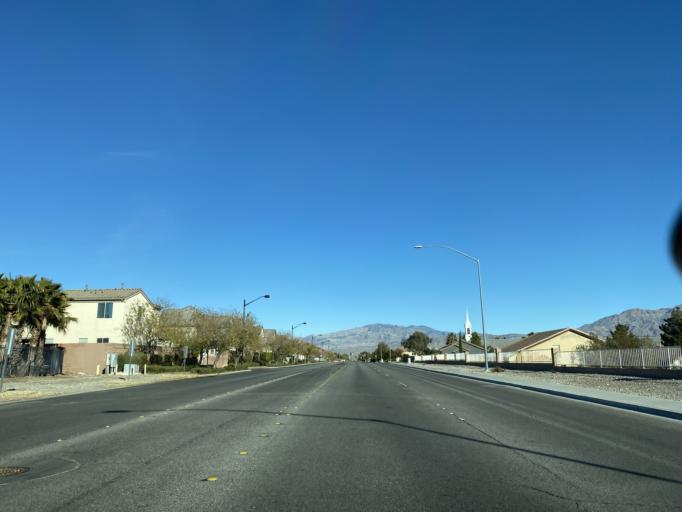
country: US
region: Nevada
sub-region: Clark County
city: Summerlin South
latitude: 36.2949
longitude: -115.2786
